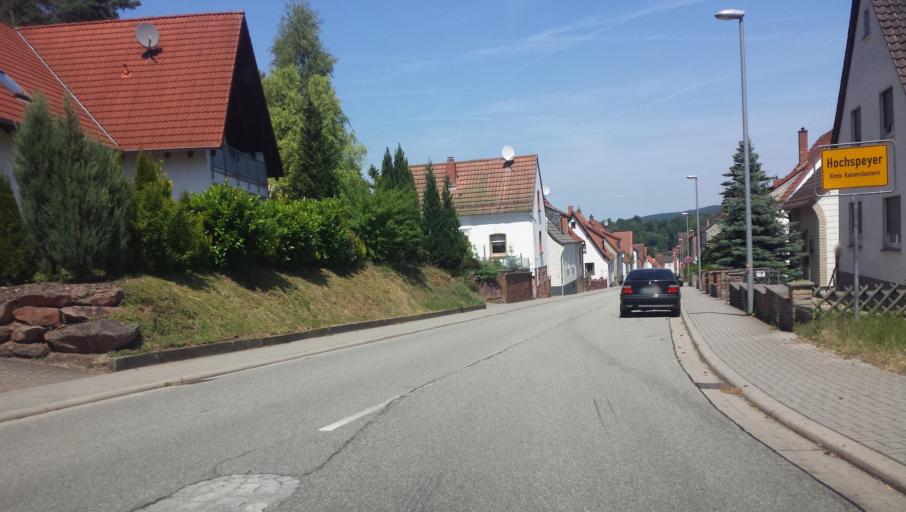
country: DE
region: Rheinland-Pfalz
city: Hochspeyer
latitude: 49.4361
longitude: 7.8897
